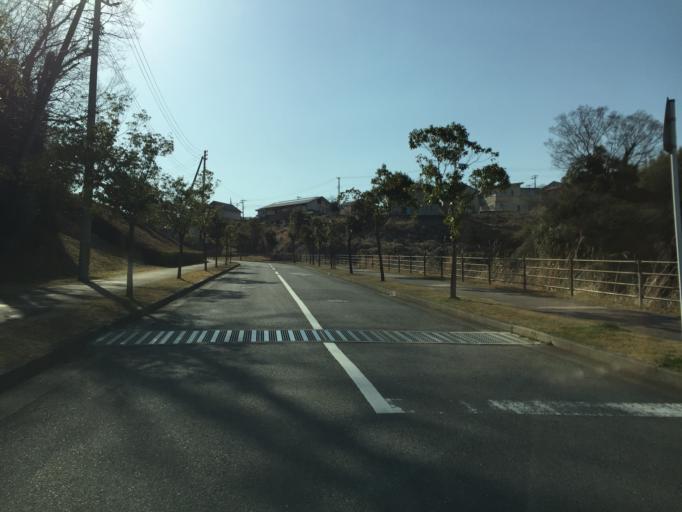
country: JP
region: Fukushima
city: Iwaki
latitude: 36.9648
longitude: 140.8708
